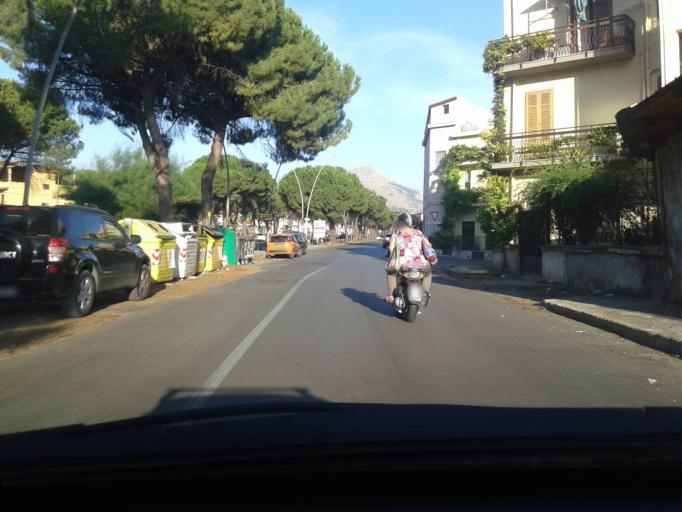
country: IT
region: Sicily
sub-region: Palermo
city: Villa Ciambra
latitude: 38.0867
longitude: 13.3505
